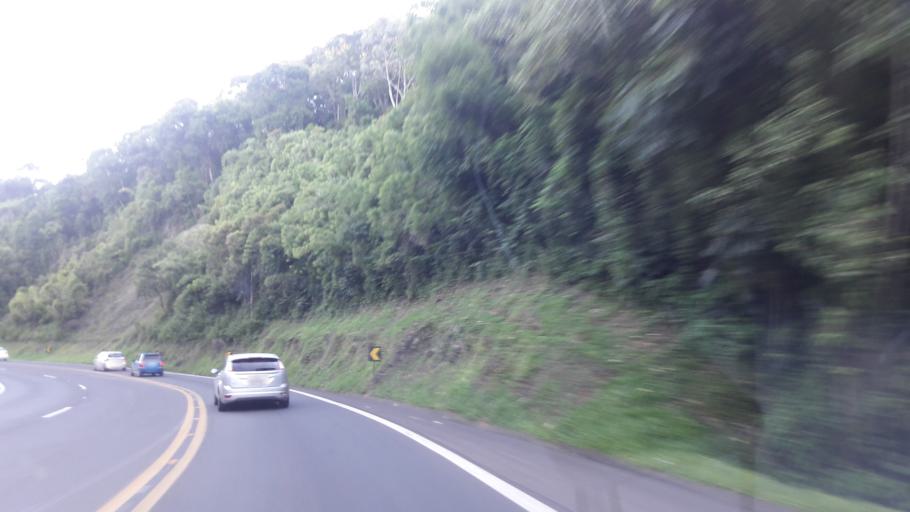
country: BR
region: Parana
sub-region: Prudentopolis
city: Prudentopolis
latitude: -25.3100
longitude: -51.2085
